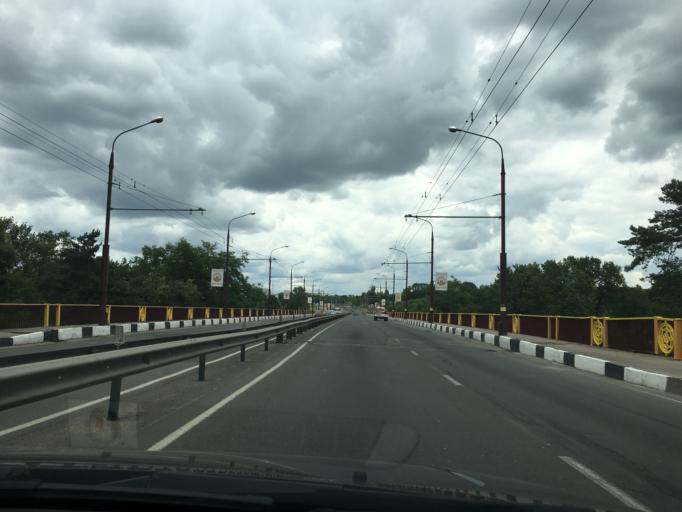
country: BY
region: Grodnenskaya
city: Hrodna
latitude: 53.6590
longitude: 23.8588
